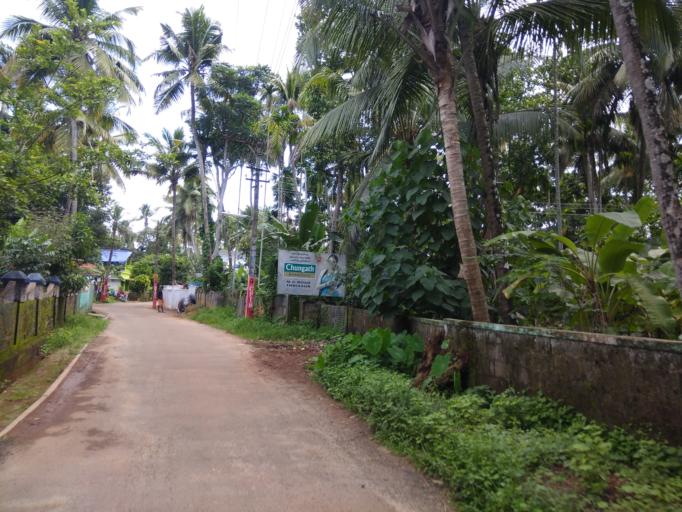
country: IN
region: Kerala
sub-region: Thrissur District
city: Trichur
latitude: 10.5376
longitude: 76.1426
